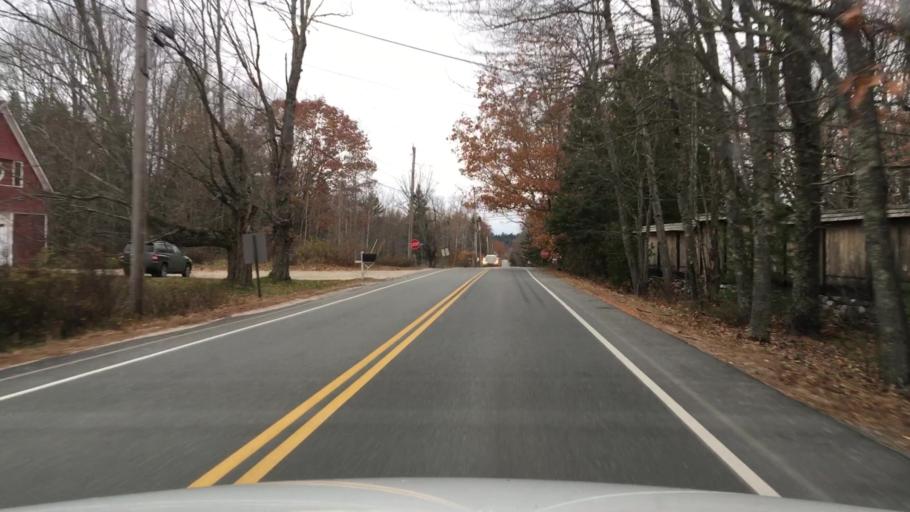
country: US
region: Maine
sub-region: Hancock County
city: Sedgwick
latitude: 44.4139
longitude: -68.6069
